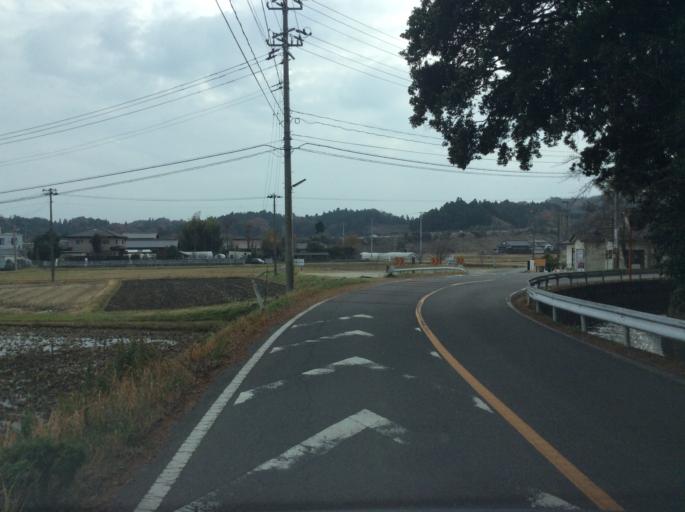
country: JP
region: Fukushima
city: Iwaki
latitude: 37.0526
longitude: 140.9404
